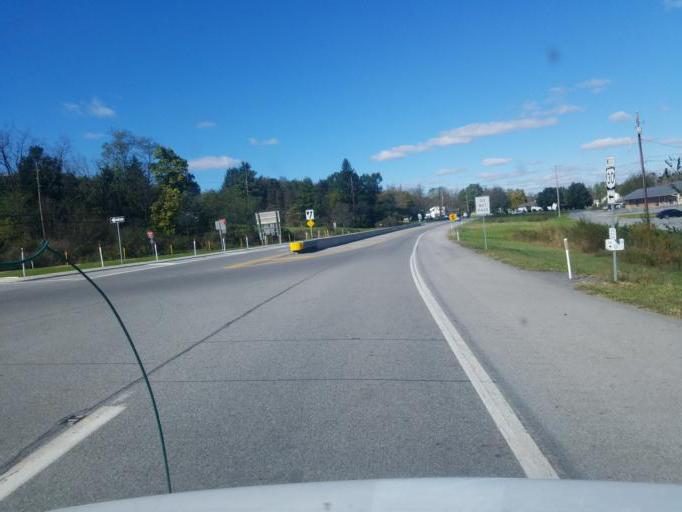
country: US
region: Pennsylvania
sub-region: Bedford County
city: Bedford
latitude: 40.0366
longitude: -78.5226
